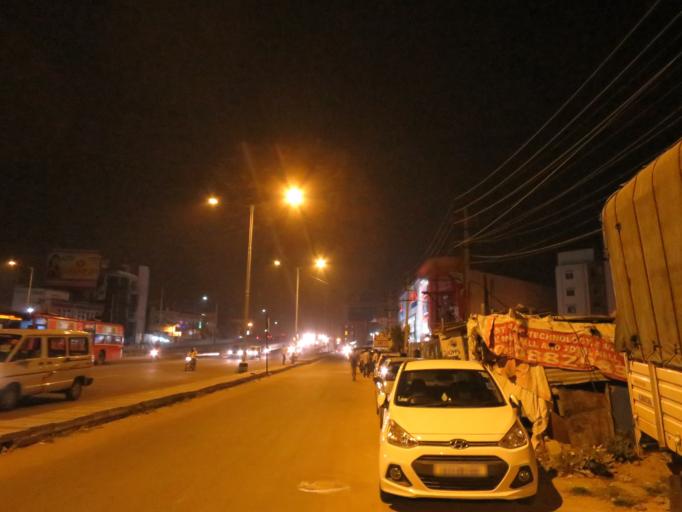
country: IN
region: Karnataka
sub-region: Bangalore Urban
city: Bangalore
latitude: 12.9886
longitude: 77.6894
